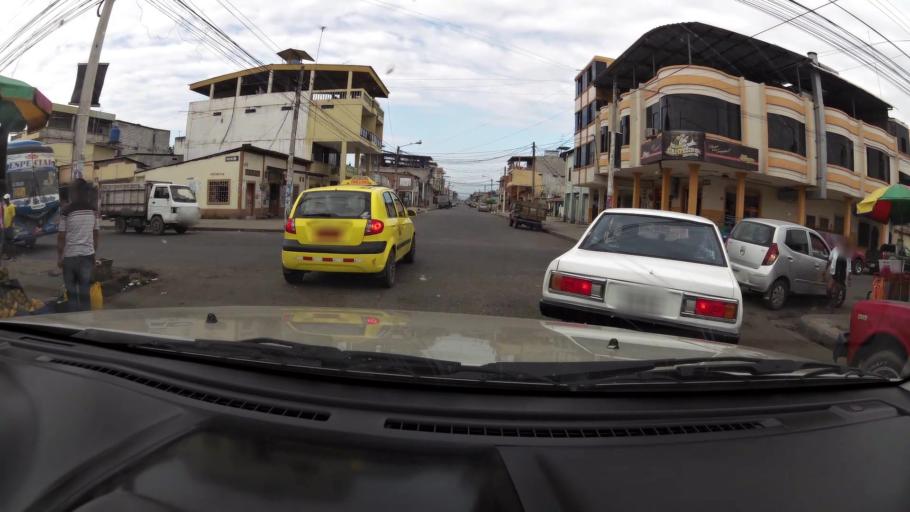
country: EC
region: El Oro
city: Machala
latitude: -3.2554
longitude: -79.9556
